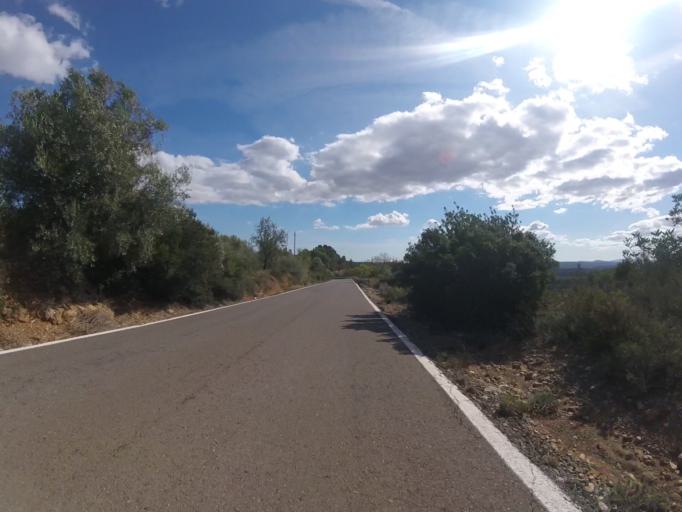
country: ES
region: Valencia
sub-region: Provincia de Castello
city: Cuevas de Vinroma
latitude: 40.3789
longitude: 0.1112
